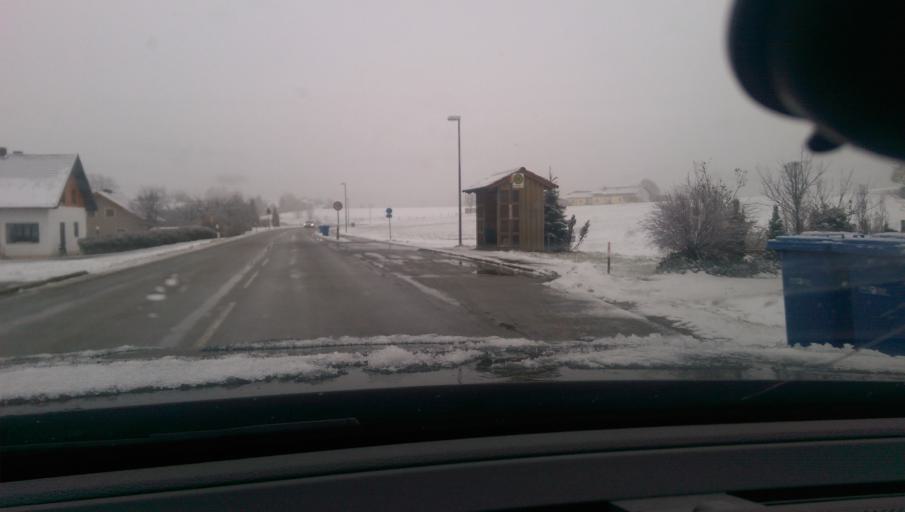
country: DE
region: Bavaria
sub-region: Lower Bavaria
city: Haselbach
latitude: 48.6578
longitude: 13.3990
